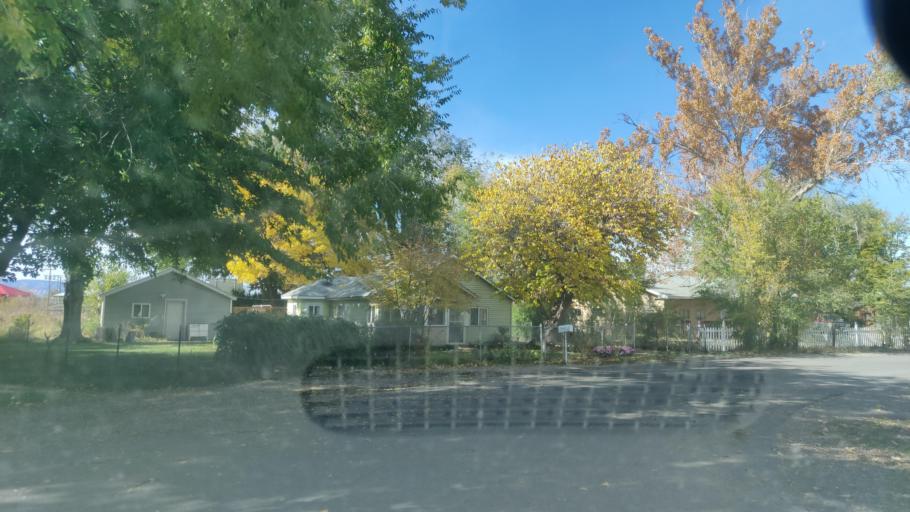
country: US
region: Colorado
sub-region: Mesa County
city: Fruitvale
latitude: 39.0796
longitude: -108.5168
